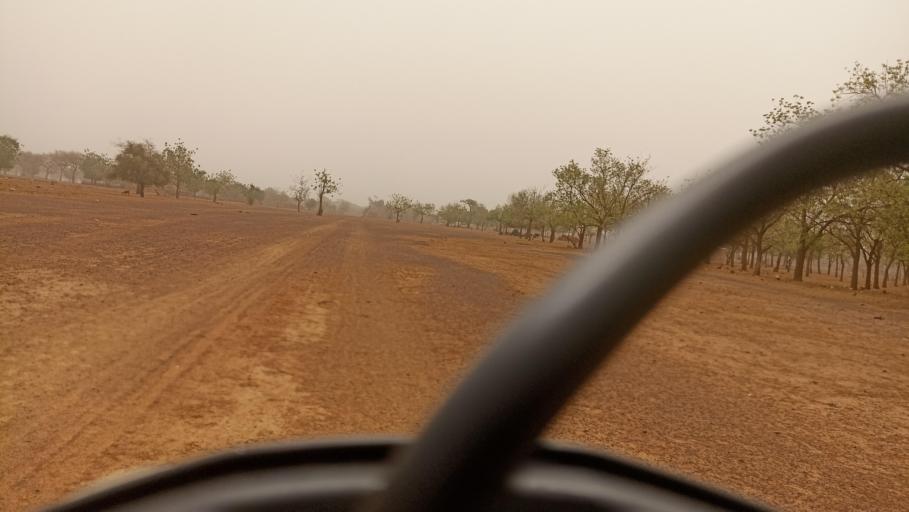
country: BF
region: Nord
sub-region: Province du Zondoma
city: Gourcy
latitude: 13.2488
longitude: -2.5940
